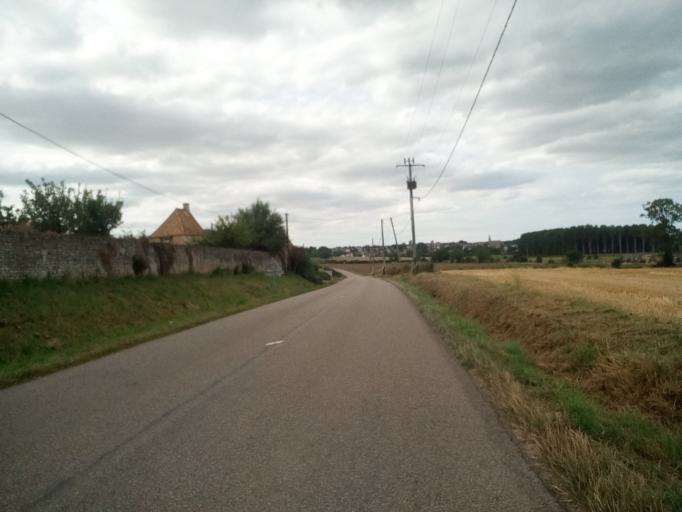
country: FR
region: Lower Normandy
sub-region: Departement du Calvados
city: Troarn
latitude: 49.1714
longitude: -0.1644
